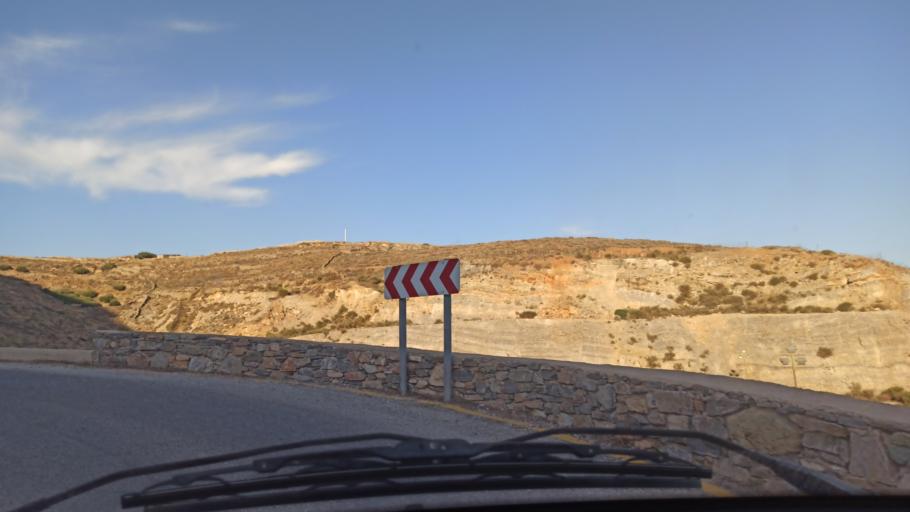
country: GR
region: South Aegean
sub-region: Nomos Kykladon
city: Ano Syros
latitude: 37.4537
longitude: 24.9365
